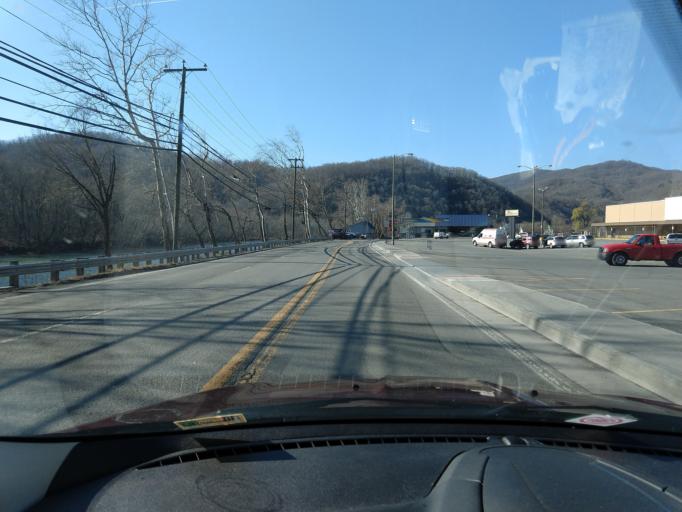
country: US
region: West Virginia
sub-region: Summers County
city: Hinton
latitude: 37.6596
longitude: -80.8914
